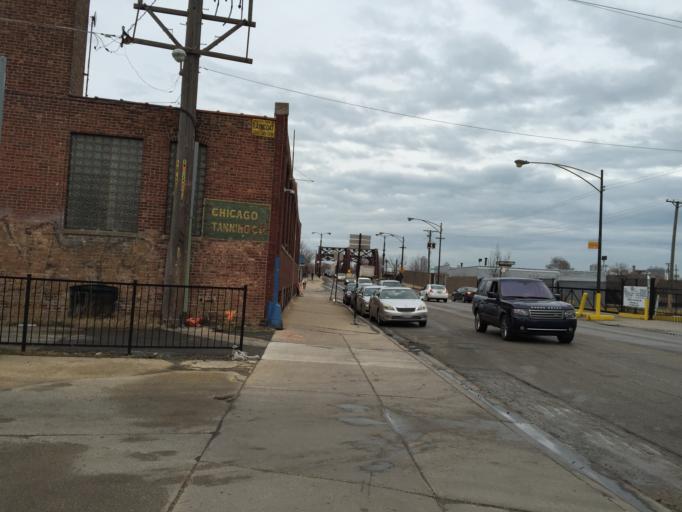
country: US
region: Illinois
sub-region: Cook County
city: Chicago
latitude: 41.9166
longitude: -87.6661
